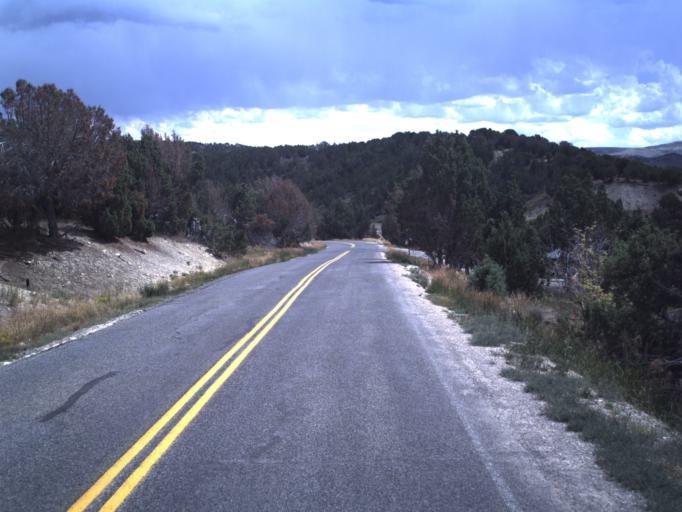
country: US
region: Utah
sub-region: Summit County
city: Oakley
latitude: 40.7828
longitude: -111.3927
